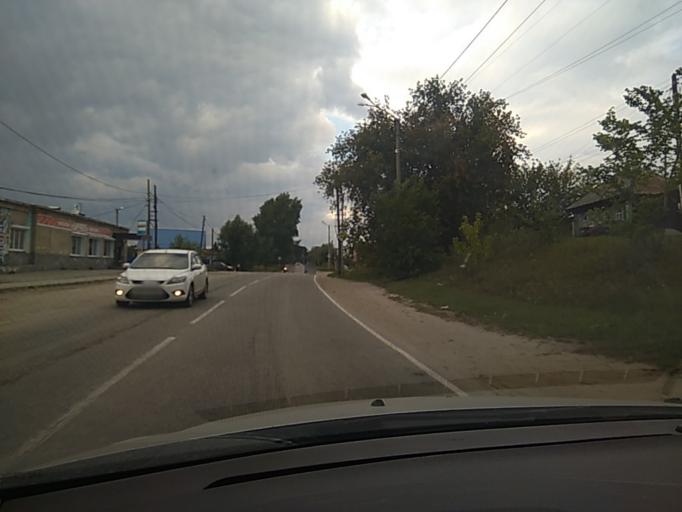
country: RU
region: Chelyabinsk
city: Kyshtym
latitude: 55.6962
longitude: 60.5520
